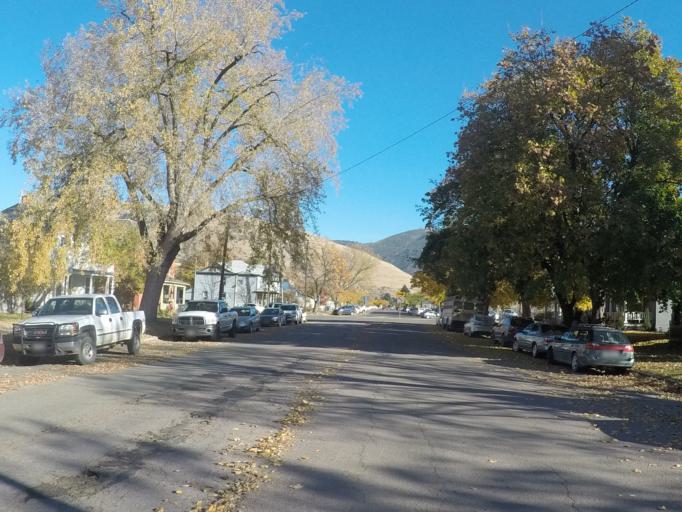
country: US
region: Montana
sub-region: Missoula County
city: Missoula
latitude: 46.8766
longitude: -113.9976
